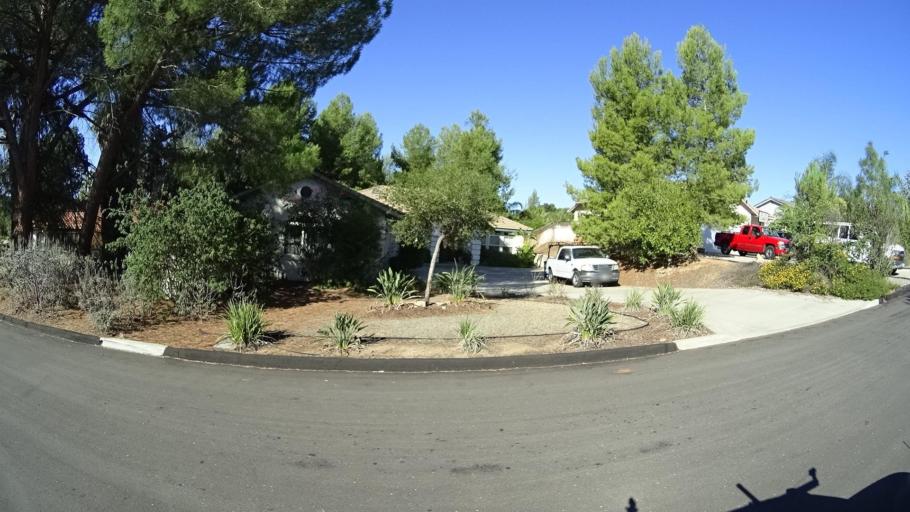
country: US
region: California
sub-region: San Diego County
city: San Diego Country Estates
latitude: 32.9968
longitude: -116.8178
